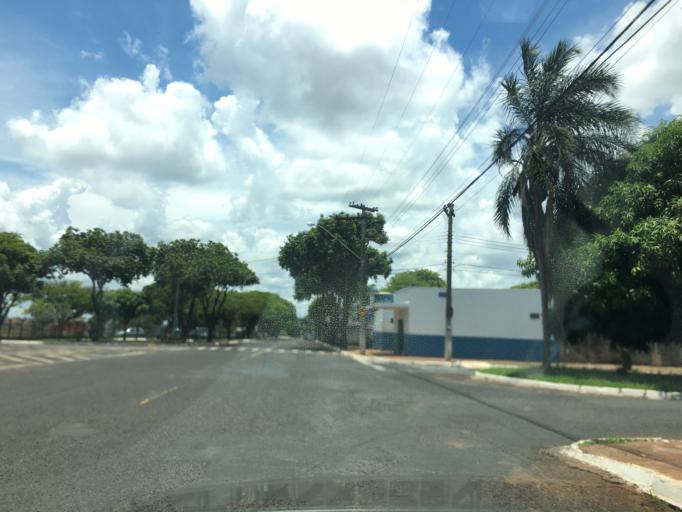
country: BR
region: Minas Gerais
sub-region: Uberlandia
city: Uberlandia
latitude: -18.9332
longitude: -48.3070
